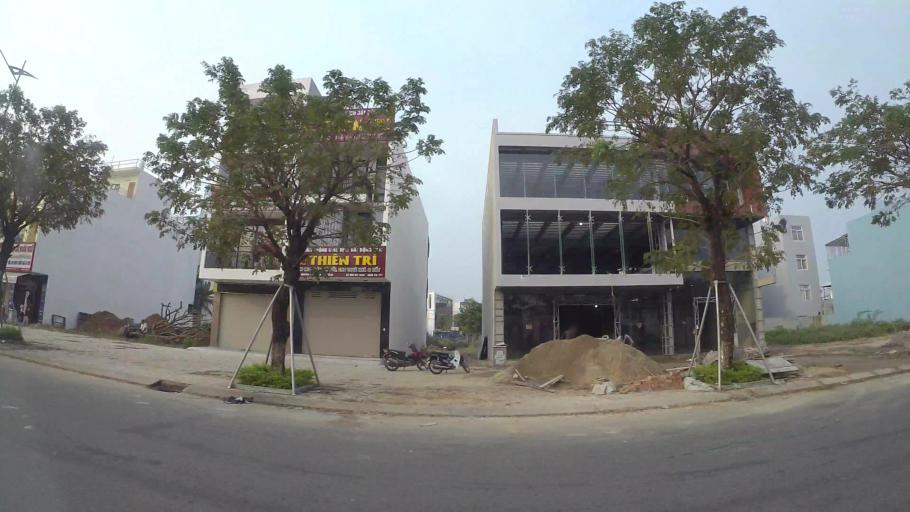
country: VN
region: Da Nang
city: Ngu Hanh Son
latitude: 16.0192
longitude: 108.2293
